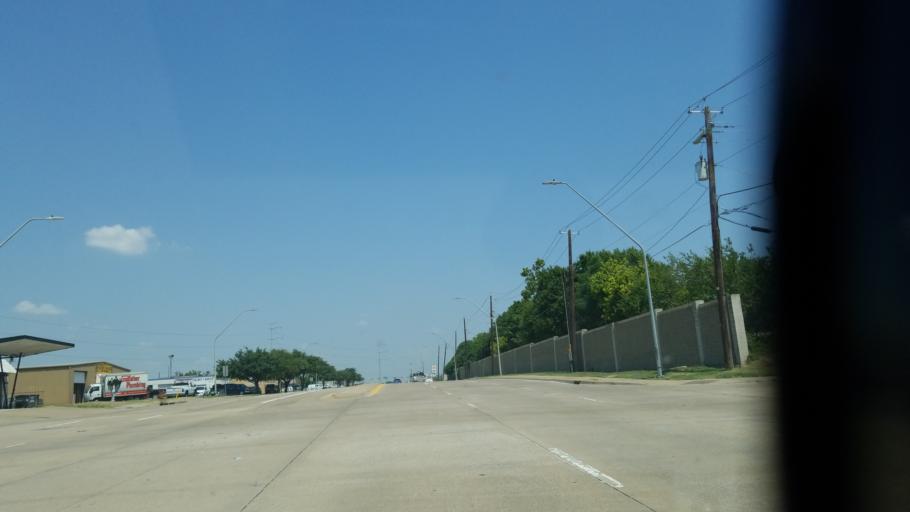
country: US
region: Texas
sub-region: Dallas County
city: Garland
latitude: 32.9177
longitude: -96.6283
